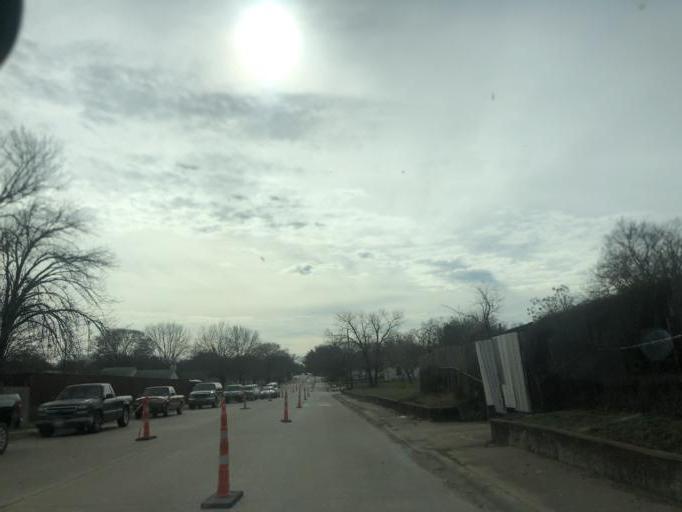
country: US
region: Texas
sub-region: Dallas County
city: Duncanville
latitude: 32.6721
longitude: -96.8292
